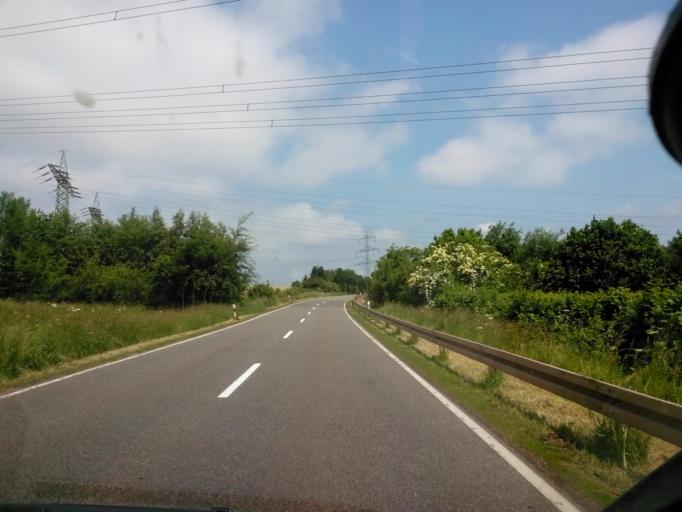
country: DE
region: Saarland
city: Eppelborn
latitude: 49.3770
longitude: 7.0000
